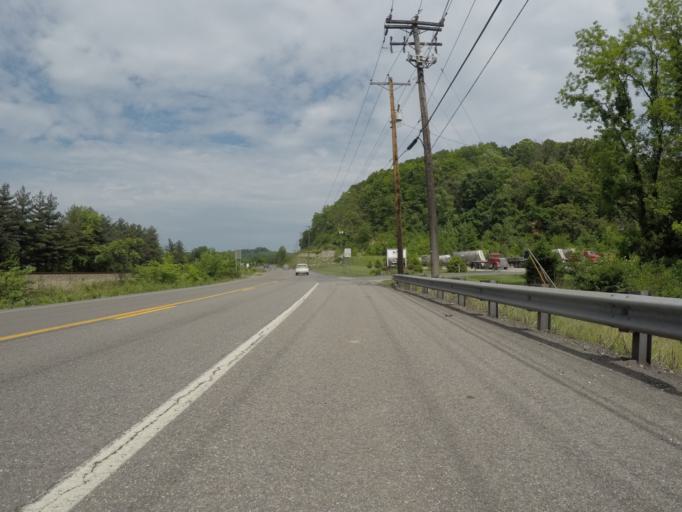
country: US
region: West Virginia
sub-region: Wayne County
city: Kenova
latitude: 38.3388
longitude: -82.5829
